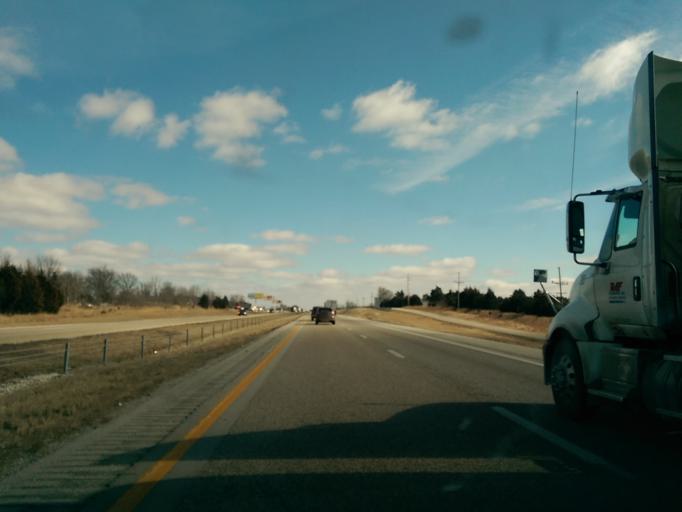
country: US
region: Missouri
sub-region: Montgomery County
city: Montgomery City
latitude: 38.9078
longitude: -91.5304
